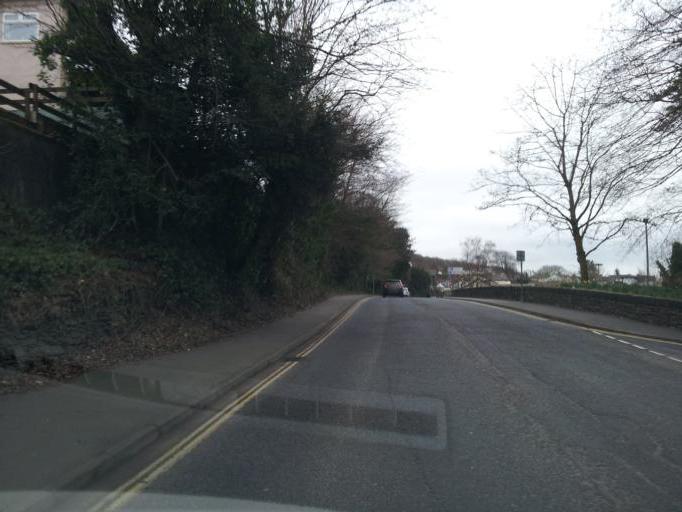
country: GB
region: England
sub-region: Cumbria
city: Windermere
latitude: 54.3670
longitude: -2.9206
